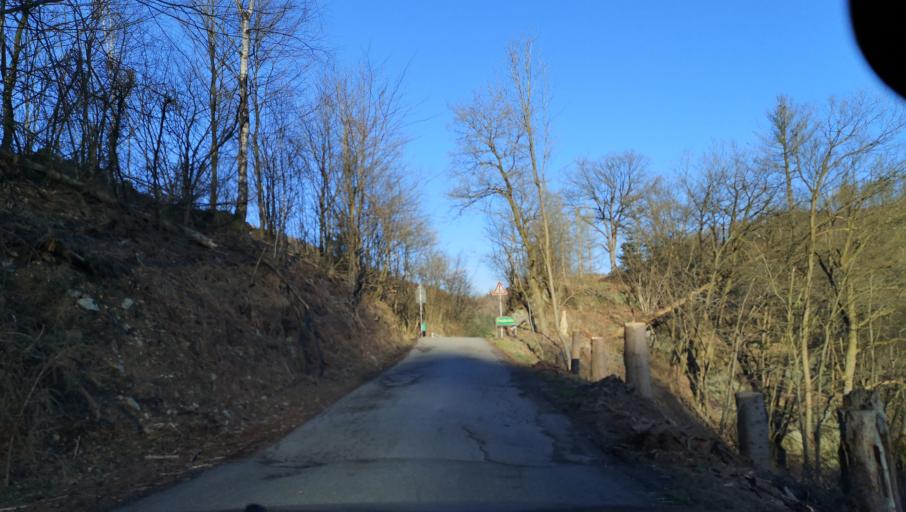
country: DE
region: North Rhine-Westphalia
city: Ennepetal
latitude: 51.2749
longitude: 7.3987
